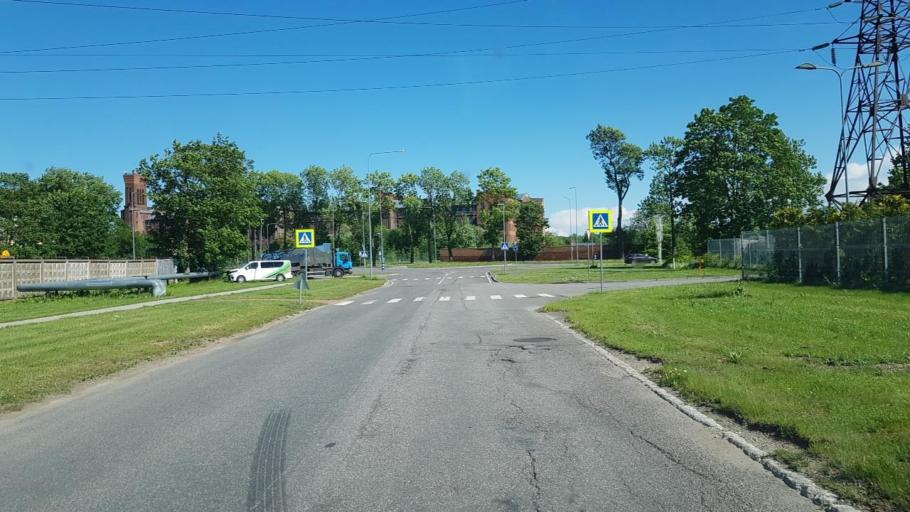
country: EE
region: Ida-Virumaa
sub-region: Narva linn
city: Narva
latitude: 59.3589
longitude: 28.1855
